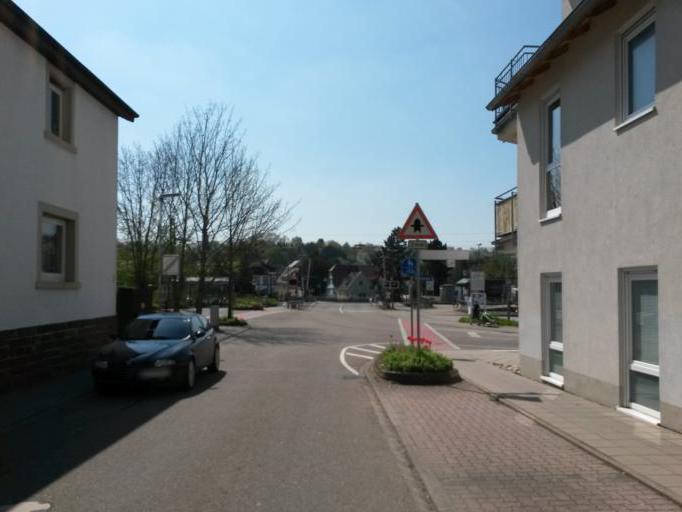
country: DE
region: Baden-Wuerttemberg
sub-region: Karlsruhe Region
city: Joehlingen
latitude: 48.9881
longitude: 8.5443
